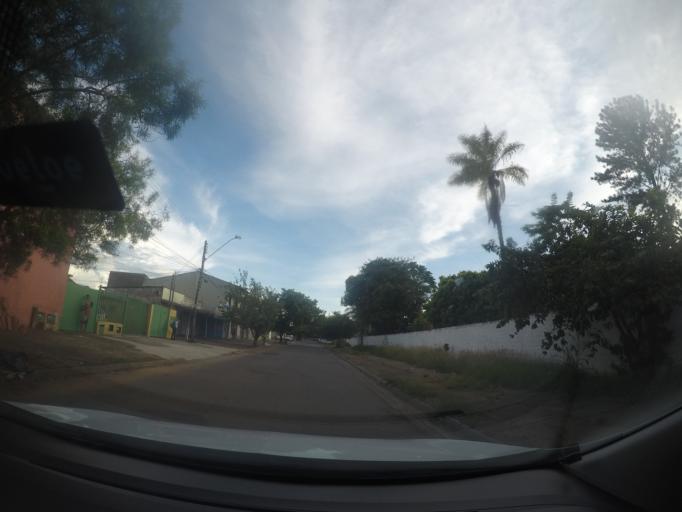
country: BR
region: Goias
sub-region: Goiania
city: Goiania
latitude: -16.6861
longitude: -49.3190
